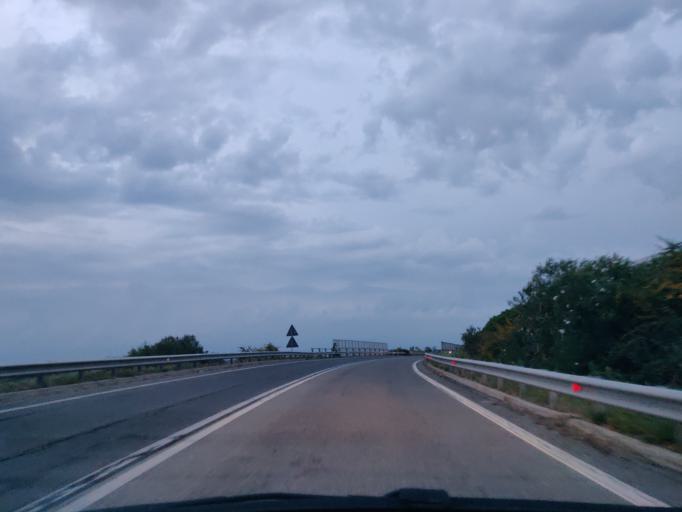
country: IT
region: Latium
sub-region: Provincia di Viterbo
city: Vetralla
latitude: 42.3737
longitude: 12.0524
